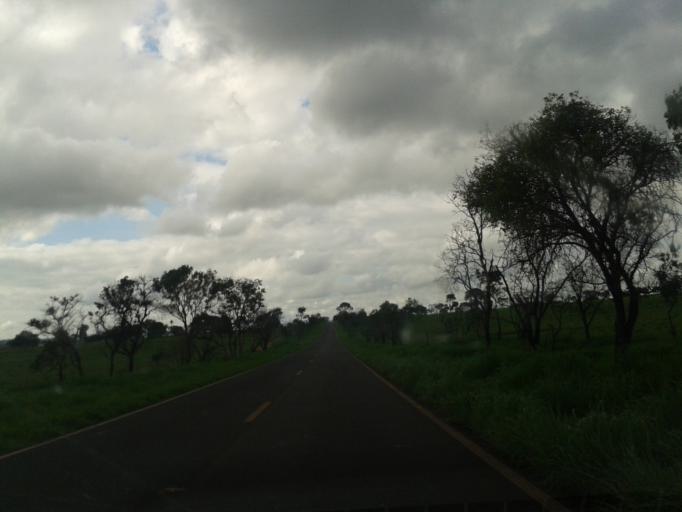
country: BR
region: Minas Gerais
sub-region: Ituiutaba
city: Ituiutaba
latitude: -19.0537
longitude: -49.7668
